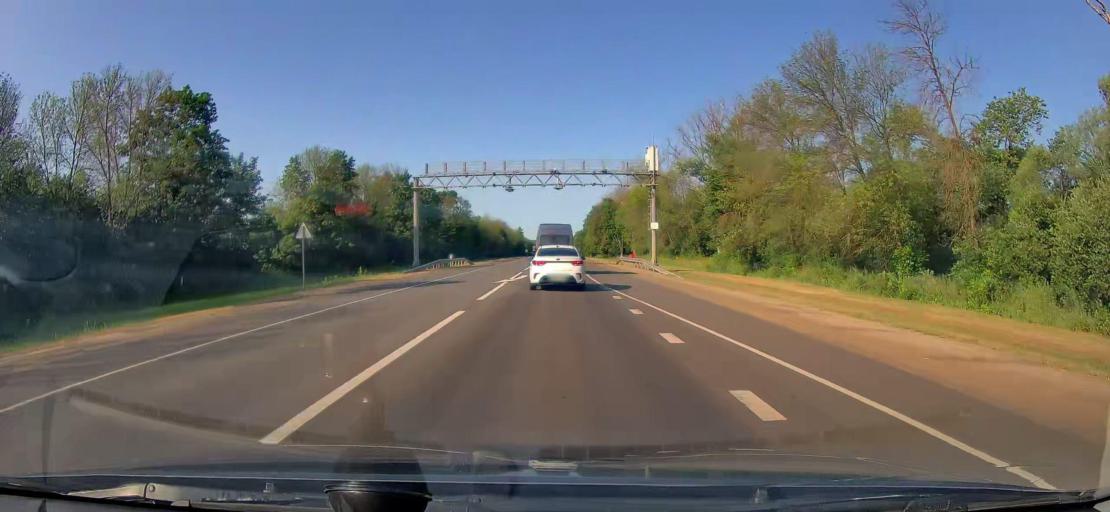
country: RU
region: Orjol
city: Mtsensk
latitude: 53.2054
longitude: 36.4465
